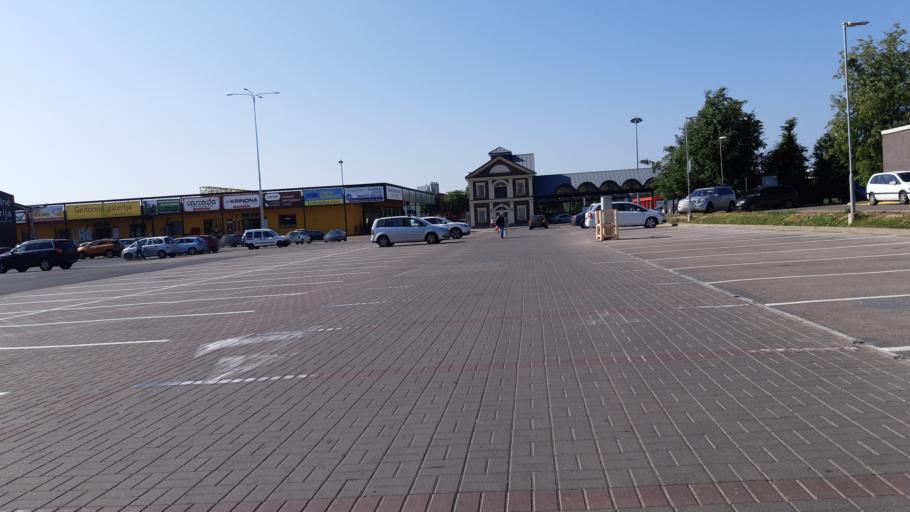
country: LT
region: Kauno apskritis
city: Dainava (Kaunas)
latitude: 54.9165
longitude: 23.9870
